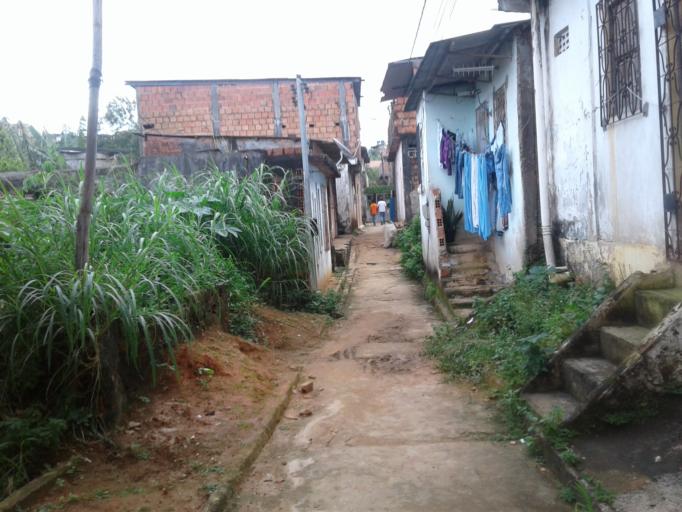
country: BR
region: Bahia
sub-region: Salvador
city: Salvador
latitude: -12.9086
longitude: -38.4730
